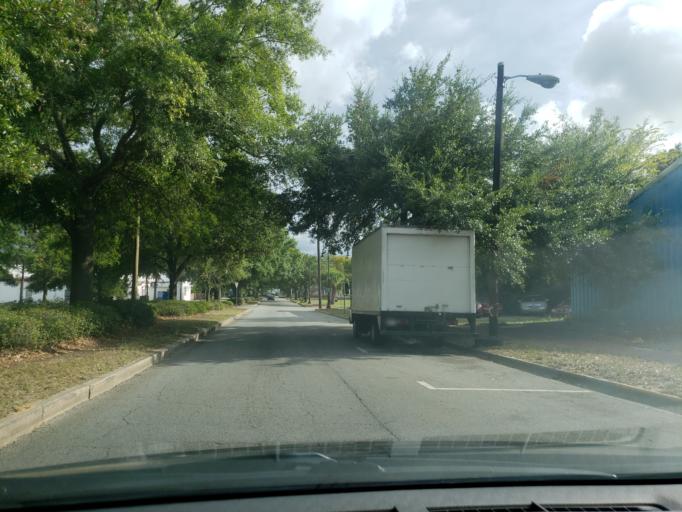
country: US
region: Georgia
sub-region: Chatham County
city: Savannah
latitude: 32.0524
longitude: -81.1077
